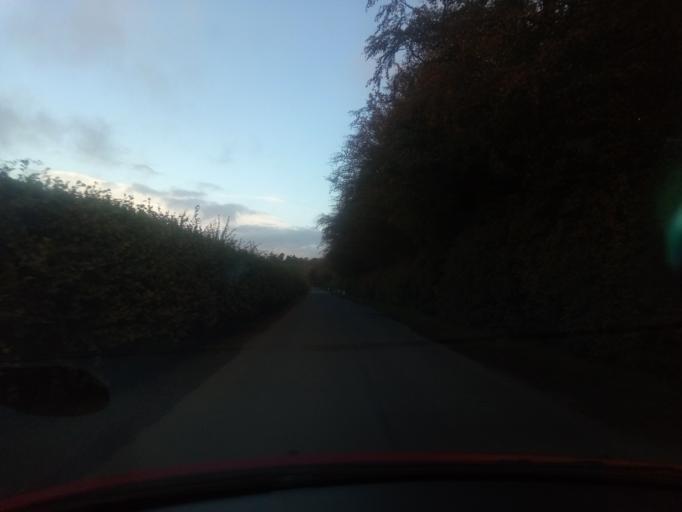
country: GB
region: Scotland
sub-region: The Scottish Borders
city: Jedburgh
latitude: 55.3848
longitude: -2.6429
